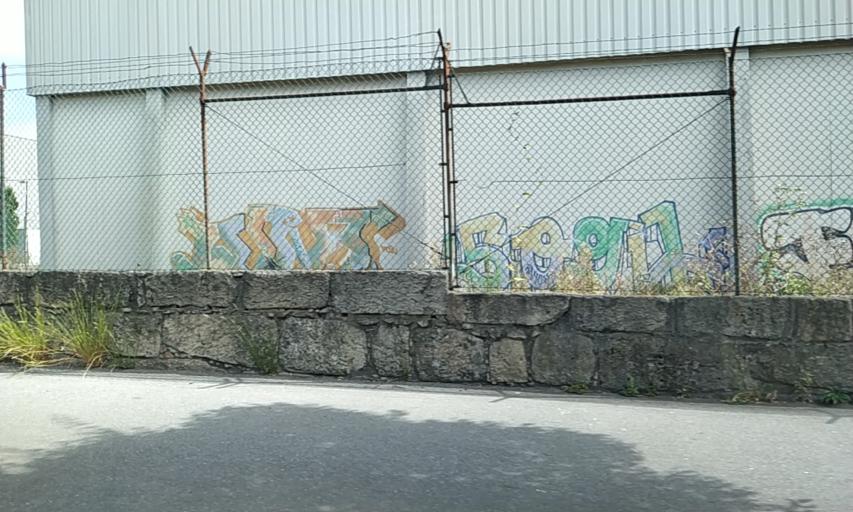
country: PT
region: Porto
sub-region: Matosinhos
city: Senhora da Hora
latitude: 41.1742
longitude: -8.6450
